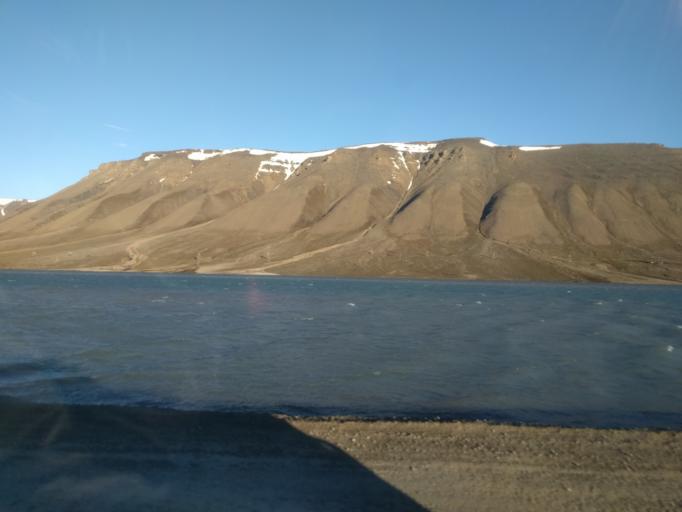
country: SJ
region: Svalbard
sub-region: Spitsbergen
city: Longyearbyen
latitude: 78.2109
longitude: 15.7603
